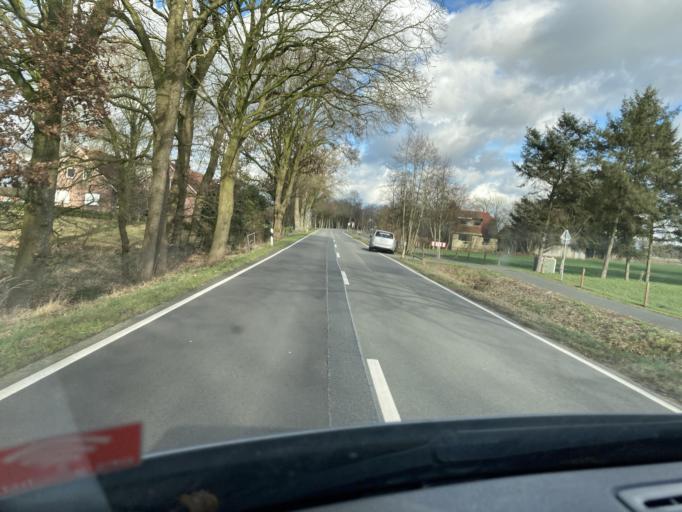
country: DE
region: Lower Saxony
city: Friedeburg
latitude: 53.3682
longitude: 7.8187
